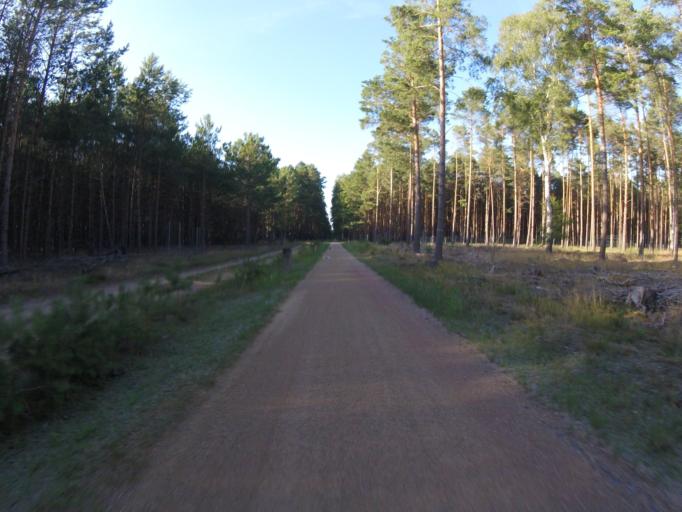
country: DE
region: Brandenburg
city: Munchehofe
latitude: 52.1966
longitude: 13.7642
